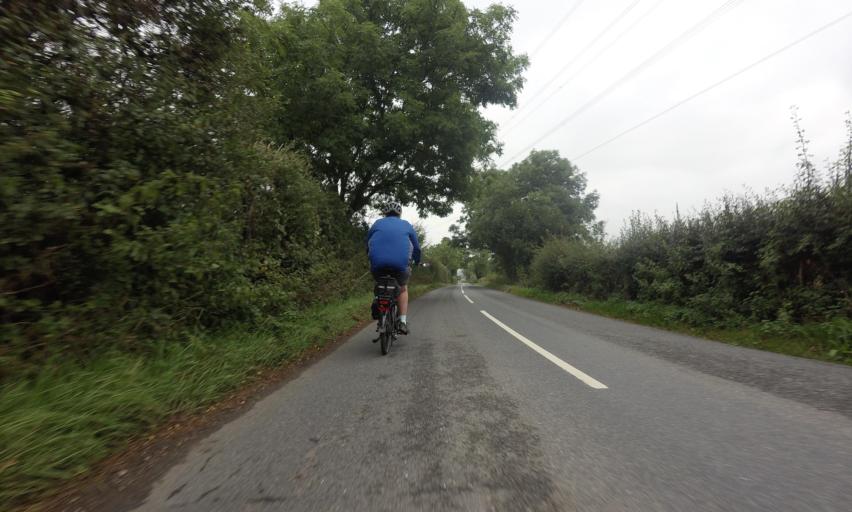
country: GB
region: England
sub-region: Gloucestershire
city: Gotherington
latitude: 51.9703
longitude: -2.0167
